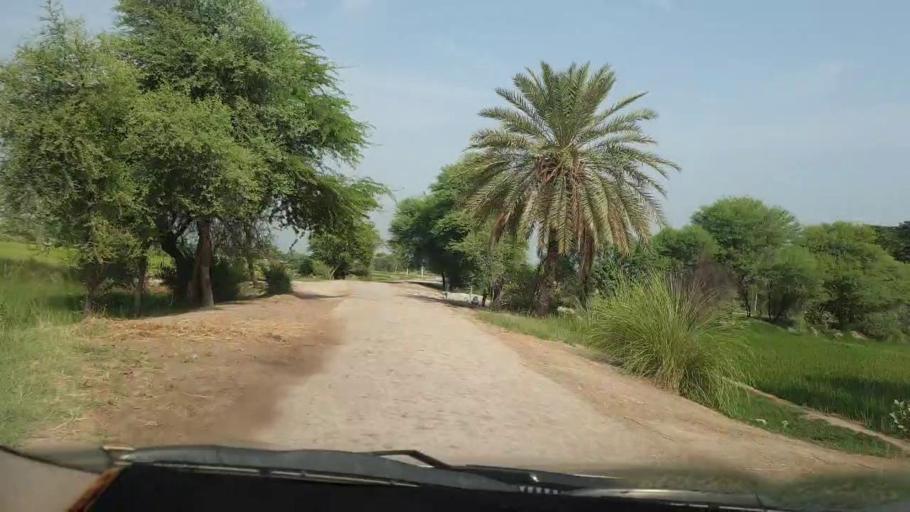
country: PK
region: Sindh
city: Goth Garelo
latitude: 27.4489
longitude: 68.0271
